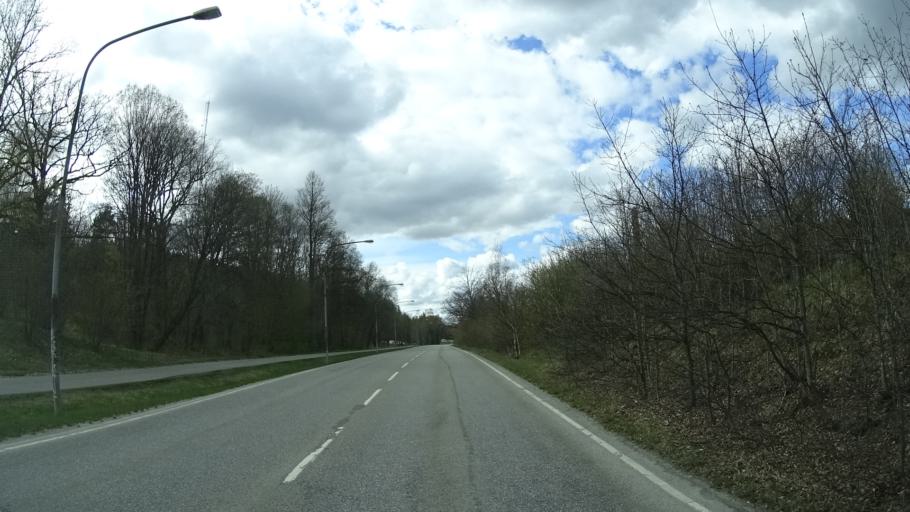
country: SE
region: Stockholm
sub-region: Nacka Kommun
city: Alta
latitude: 59.2622
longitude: 18.1502
